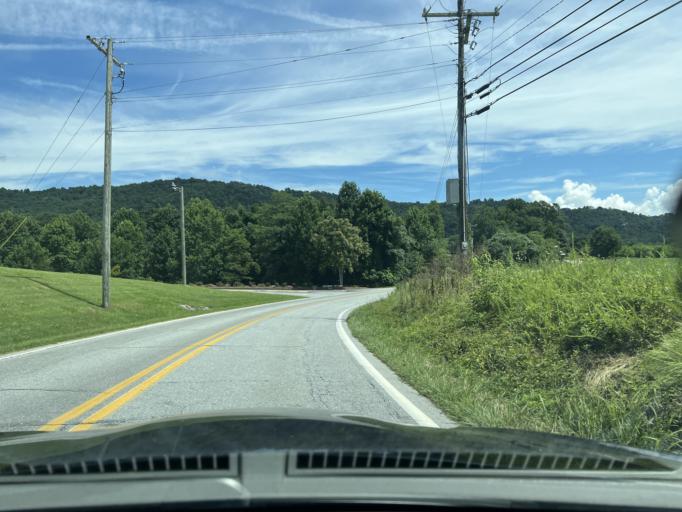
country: US
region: North Carolina
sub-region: Henderson County
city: Edneyville
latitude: 35.3910
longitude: -82.3322
